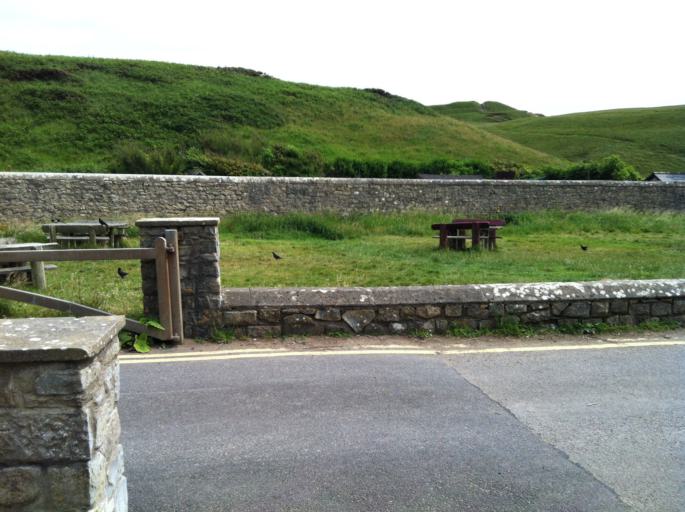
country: GB
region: Wales
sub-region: Bridgend county borough
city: Merthyr Mawr
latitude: 51.4465
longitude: -3.6047
